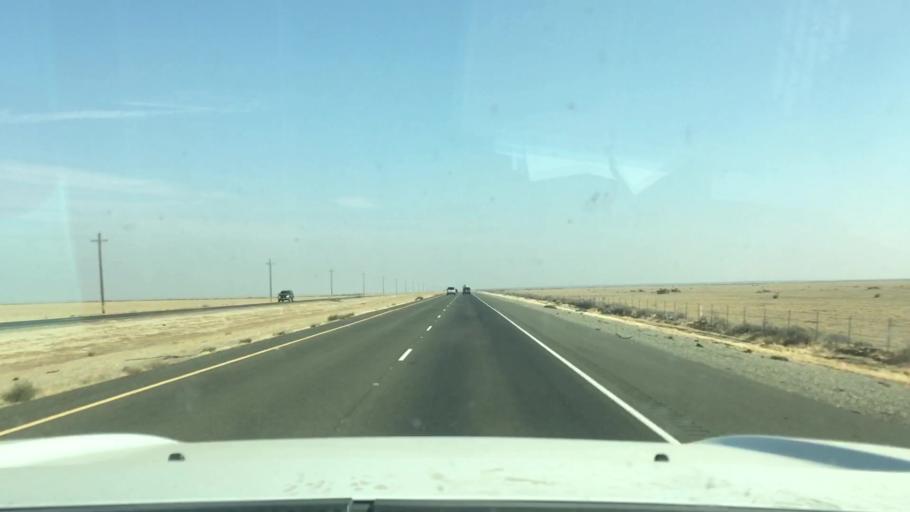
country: US
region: California
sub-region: Kern County
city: Lost Hills
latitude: 35.6156
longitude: -119.7948
